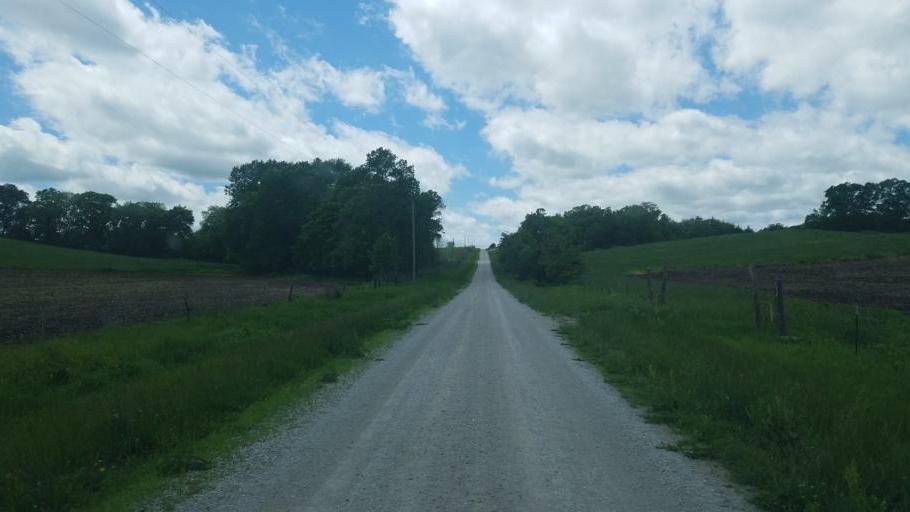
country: US
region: Iowa
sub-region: Decatur County
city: Lamoni
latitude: 40.5005
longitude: -94.0103
